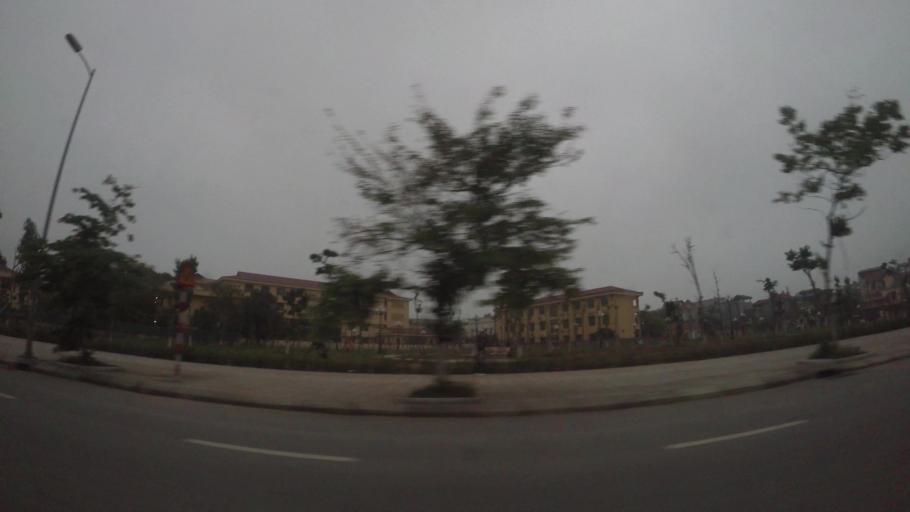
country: VN
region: Ha Noi
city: Van Dien
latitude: 20.9738
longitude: 105.8830
